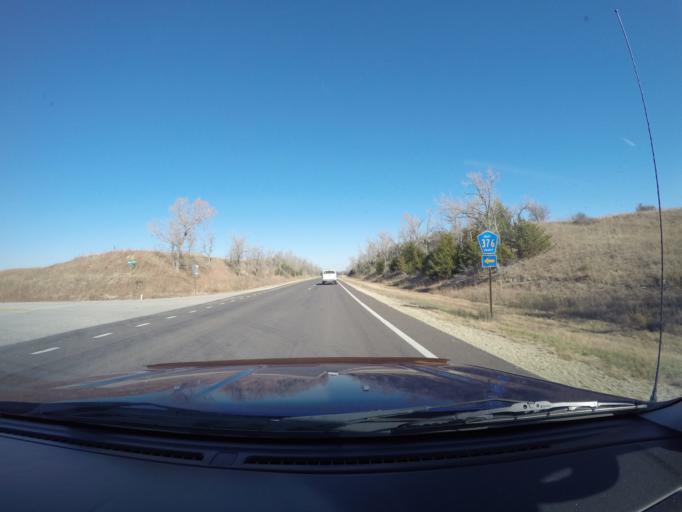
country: US
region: Kansas
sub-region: Marshall County
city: Blue Rapids
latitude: 39.4862
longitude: -96.7552
